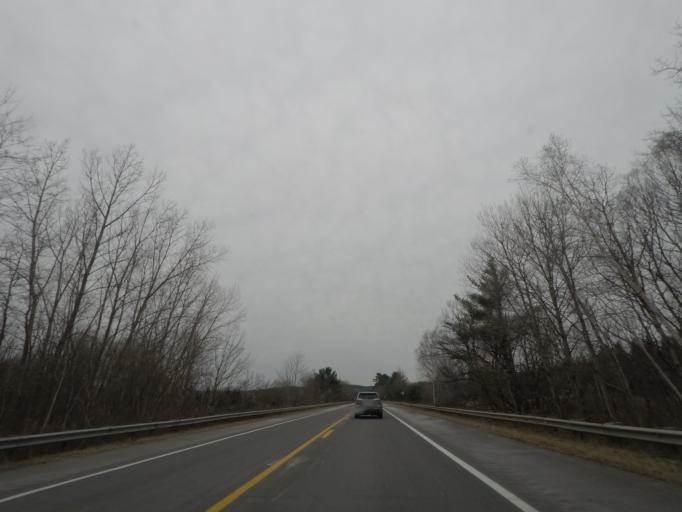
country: US
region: Massachusetts
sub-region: Berkshire County
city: Lanesborough
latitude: 42.5387
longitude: -73.3338
